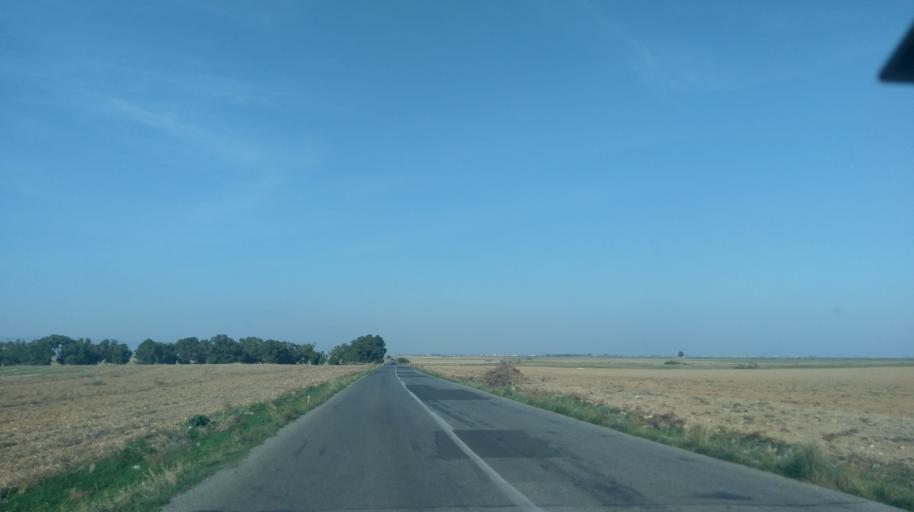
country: CY
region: Ammochostos
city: Achna
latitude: 35.1292
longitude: 33.7364
